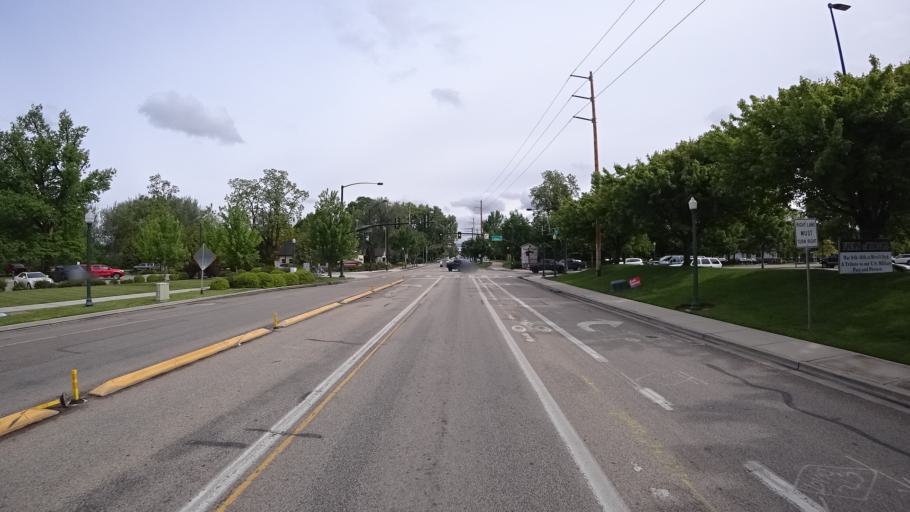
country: US
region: Idaho
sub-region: Ada County
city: Eagle
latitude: 43.6924
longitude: -116.3540
